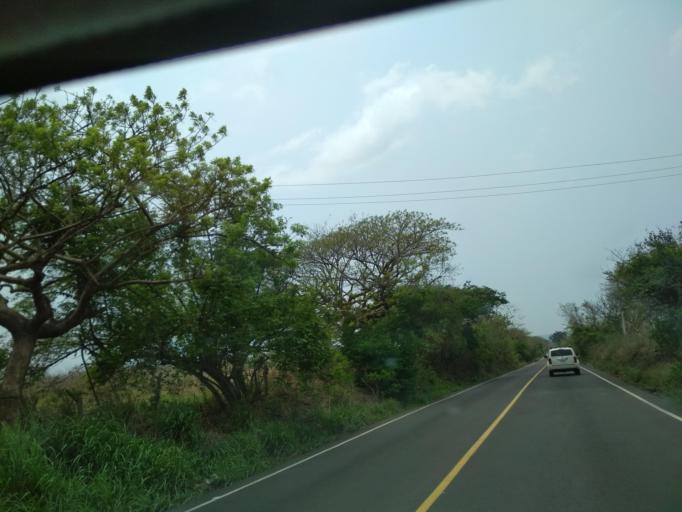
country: MX
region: Veracruz
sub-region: Veracruz
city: Delfino Victoria (Santa Fe)
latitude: 19.1597
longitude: -96.2870
